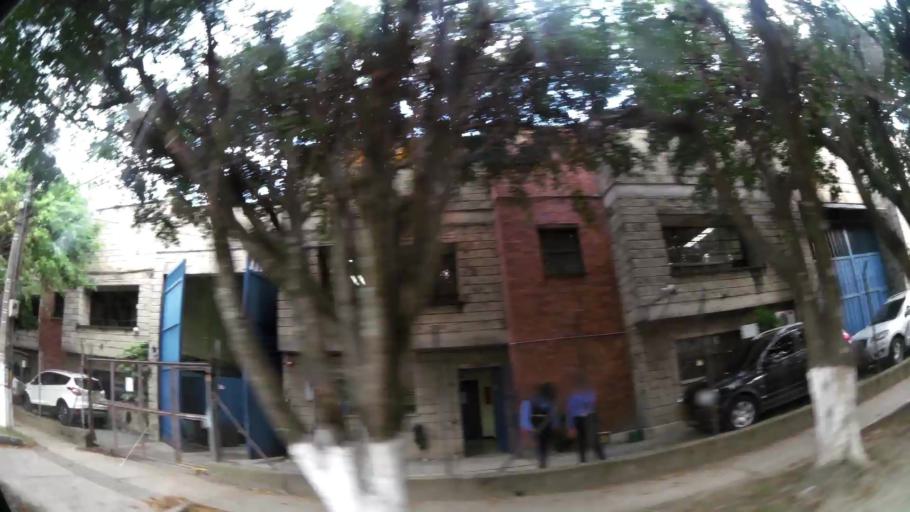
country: CO
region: Antioquia
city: Itagui
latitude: 6.2003
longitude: -75.5864
